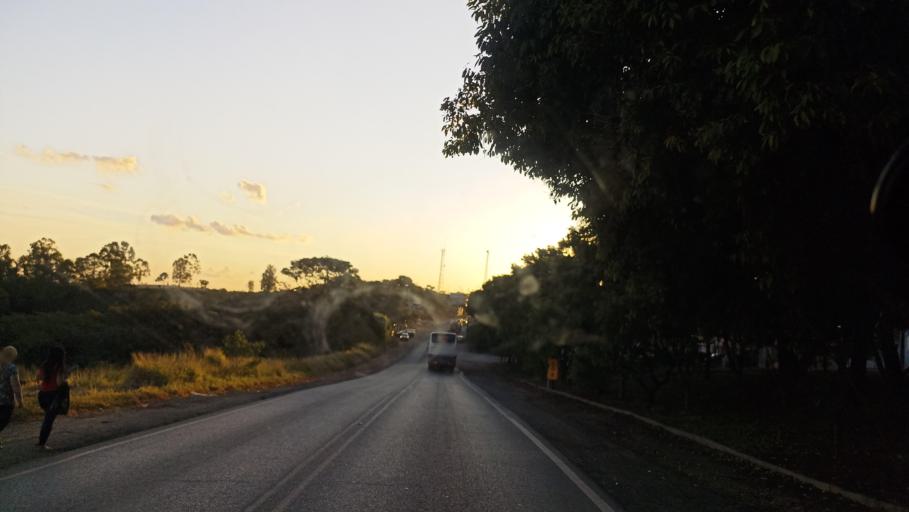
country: BR
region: Minas Gerais
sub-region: Sao Joao Del Rei
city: Sao Joao del Rei
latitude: -21.2436
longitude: -44.4077
